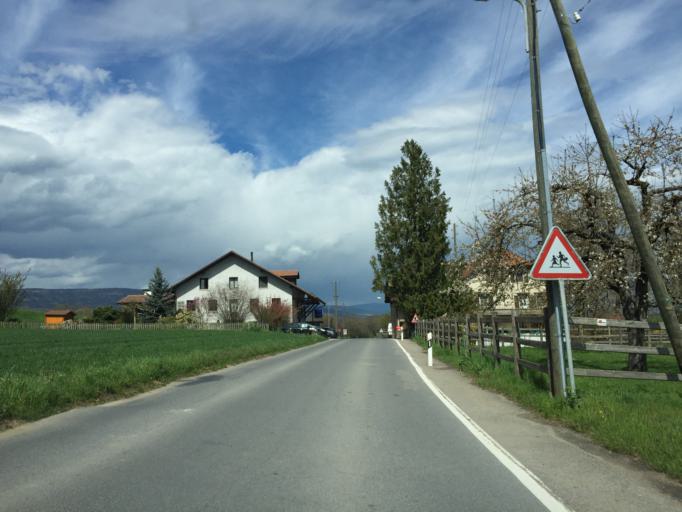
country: CH
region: Vaud
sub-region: Morges District
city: Grancy
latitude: 46.5952
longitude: 6.4612
